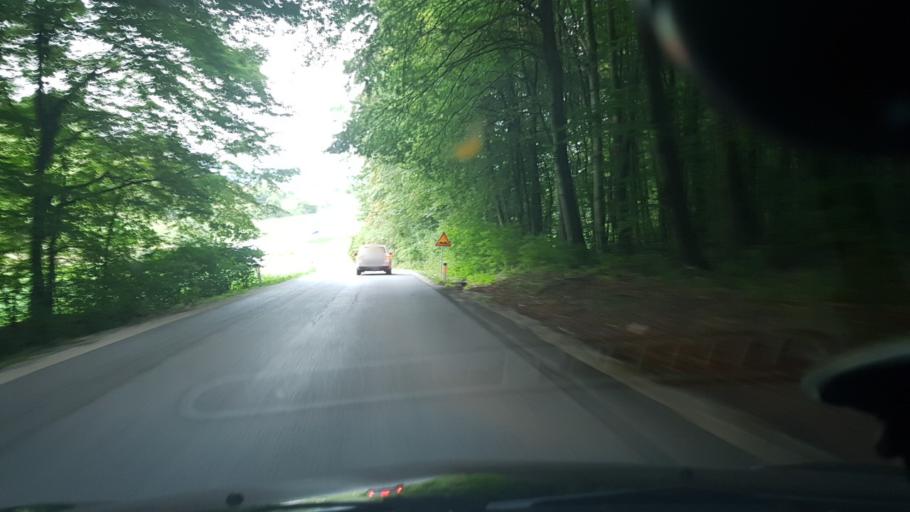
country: SI
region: Kozje
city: Kozje
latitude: 46.1061
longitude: 15.5936
